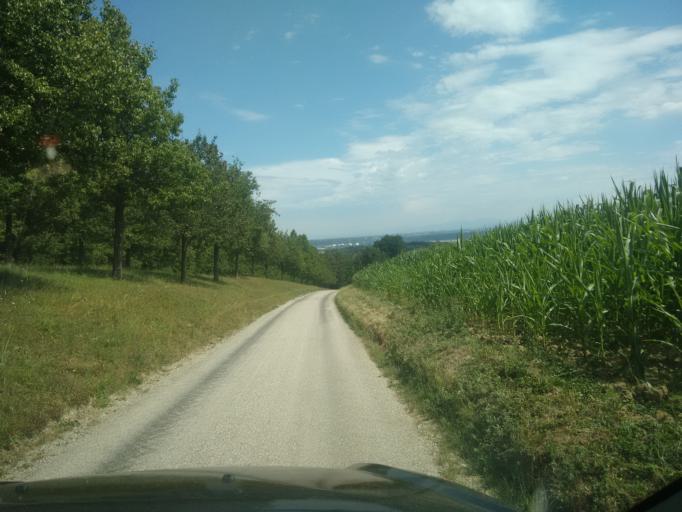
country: AT
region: Upper Austria
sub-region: Wels-Land
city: Gunskirchen
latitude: 48.1723
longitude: 13.9319
